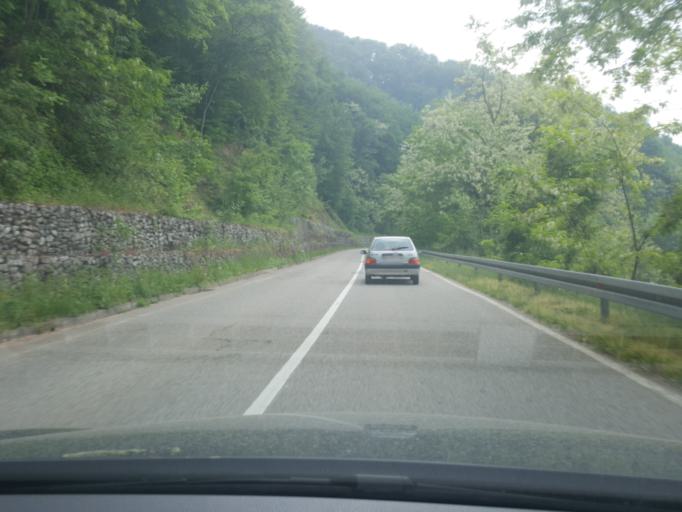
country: RS
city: Kamenica
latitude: 44.2364
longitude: 19.7241
